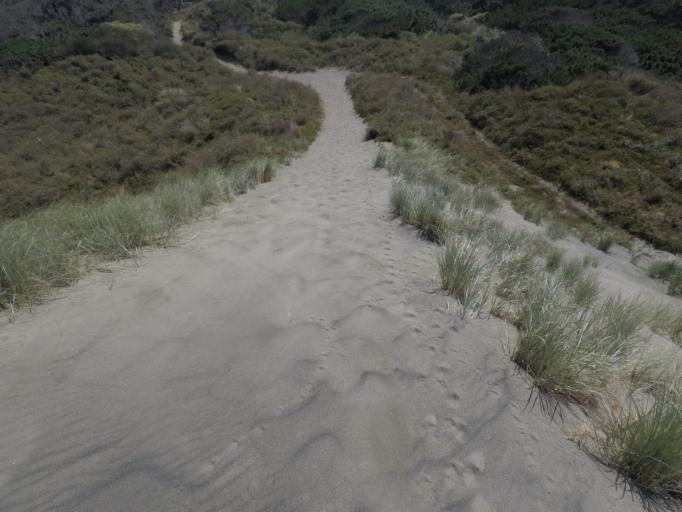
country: NZ
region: Auckland
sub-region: Auckland
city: Parakai
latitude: -36.6068
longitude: 174.2704
